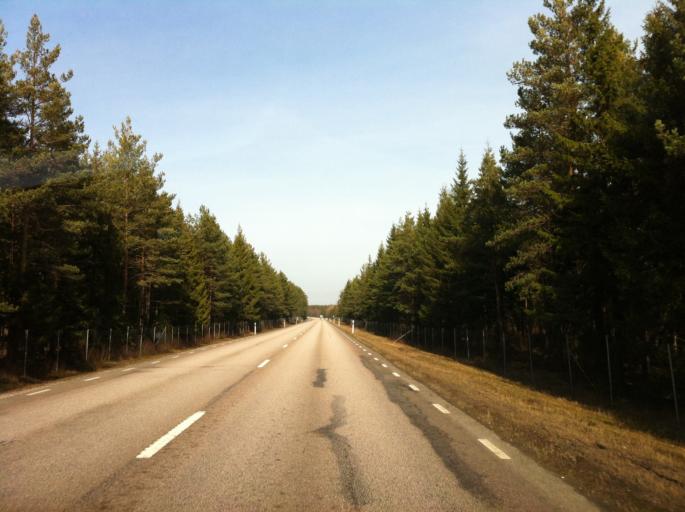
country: SE
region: Vaestra Goetaland
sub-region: Tidaholms Kommun
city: Tidaholm
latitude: 58.1082
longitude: 13.8878
